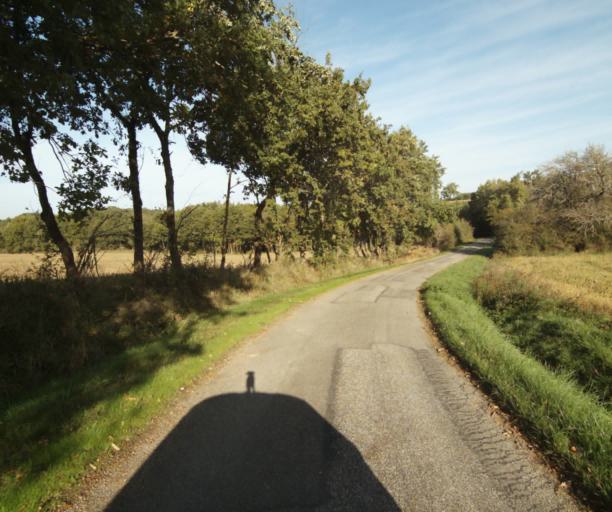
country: FR
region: Midi-Pyrenees
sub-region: Departement du Tarn-et-Garonne
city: Nohic
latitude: 43.9271
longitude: 1.4499
